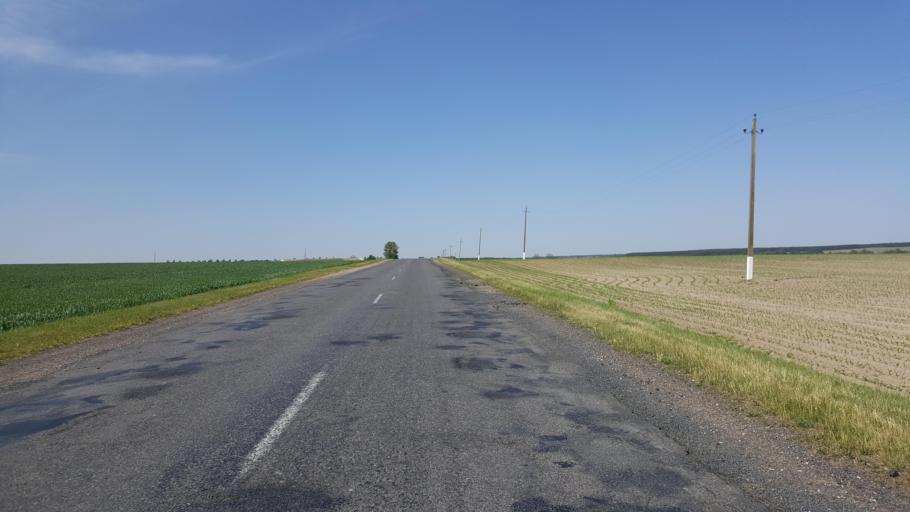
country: BY
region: Brest
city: Charnawchytsy
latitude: 52.2931
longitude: 23.6059
